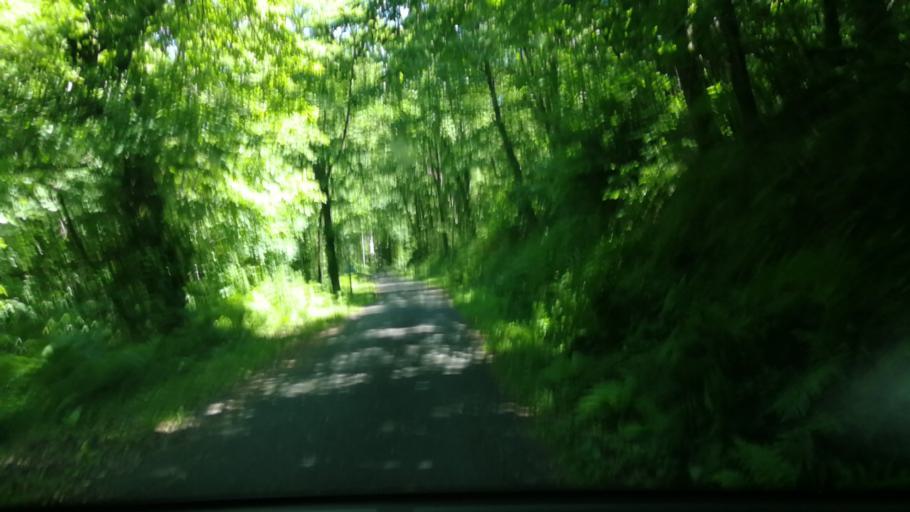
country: FR
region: Midi-Pyrenees
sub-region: Departement de l'Aveyron
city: Firmi
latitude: 44.5992
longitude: 2.3903
